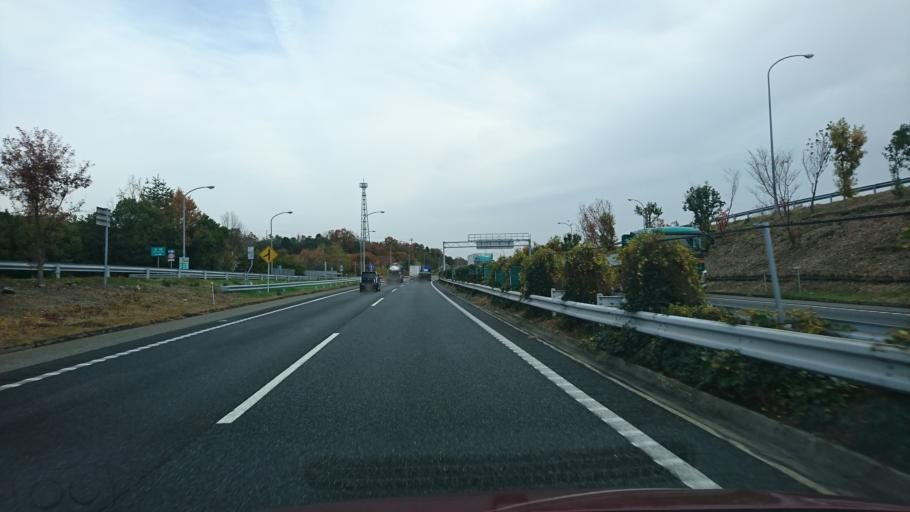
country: JP
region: Hyogo
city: Miki
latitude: 34.8169
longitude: 134.9818
